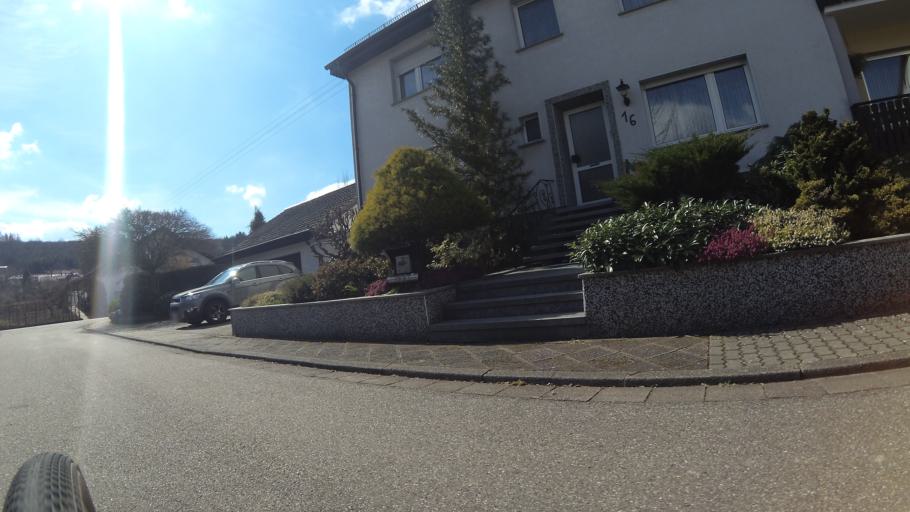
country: DE
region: Saarland
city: Rehlingen-Siersburg
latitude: 49.3529
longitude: 6.6163
